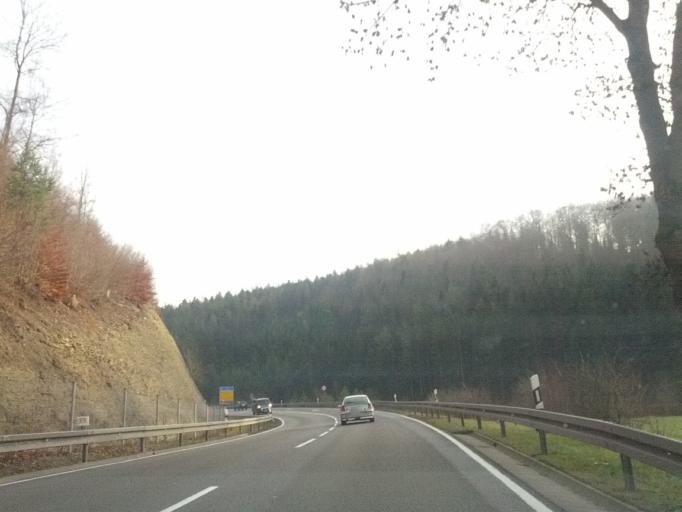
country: DE
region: Thuringia
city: Ellingshausen
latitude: 50.5857
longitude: 10.4567
